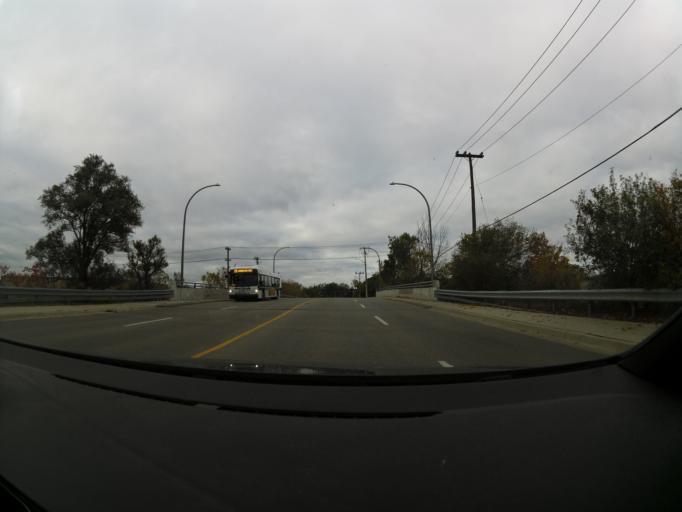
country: CA
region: Ontario
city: Kitchener
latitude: 43.4399
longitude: -80.4854
